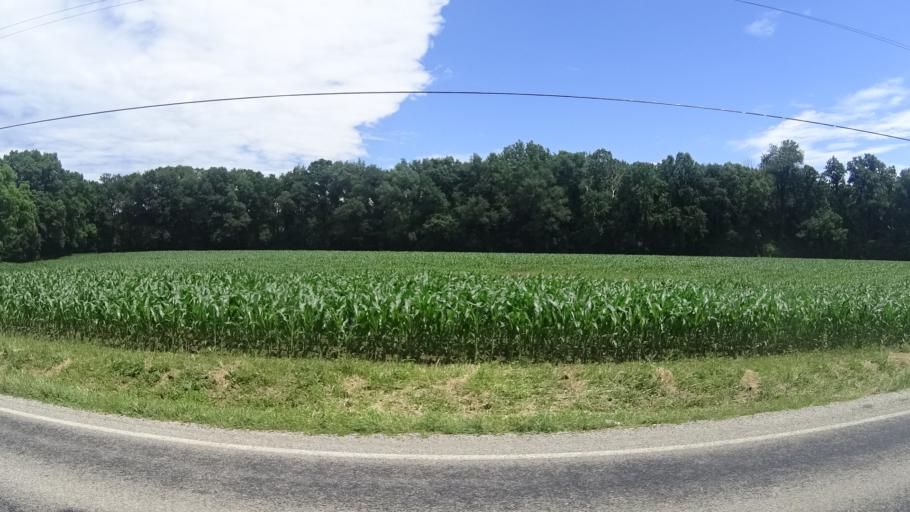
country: US
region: Ohio
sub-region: Erie County
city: Milan
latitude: 41.2891
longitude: -82.6215
